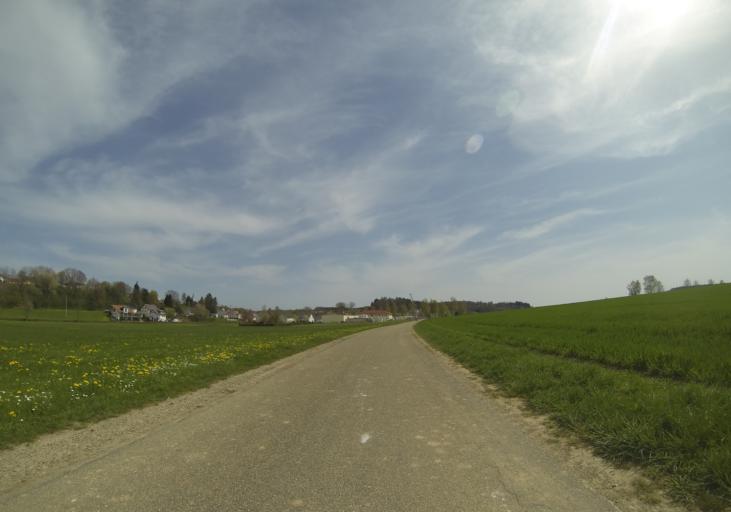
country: DE
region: Baden-Wuerttemberg
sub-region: Tuebingen Region
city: Huttisheim
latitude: 48.2638
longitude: 9.9499
